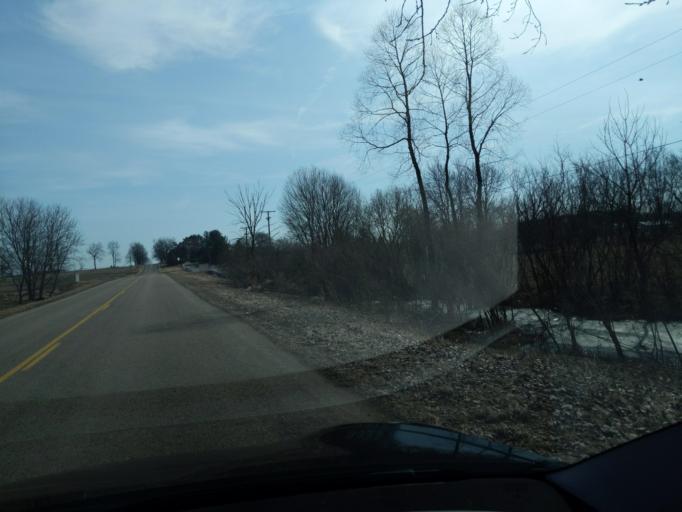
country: US
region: Michigan
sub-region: Ingham County
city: Williamston
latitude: 42.6595
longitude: -84.2462
